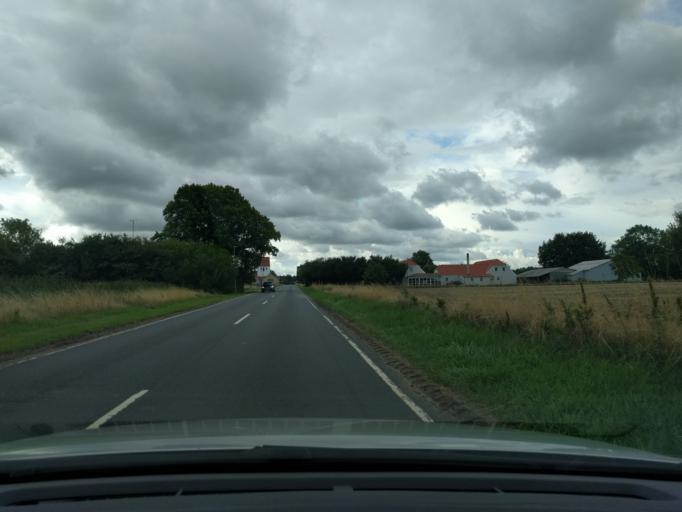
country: DK
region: South Denmark
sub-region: Nyborg Kommune
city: Ullerslev
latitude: 55.3880
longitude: 10.6666
